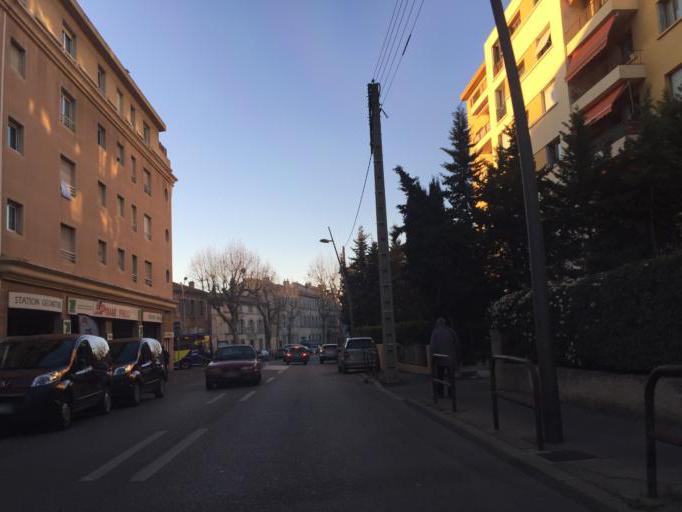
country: FR
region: Provence-Alpes-Cote d'Azur
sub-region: Departement des Bouches-du-Rhone
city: Aix-en-Provence
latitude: 43.5222
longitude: 5.4572
